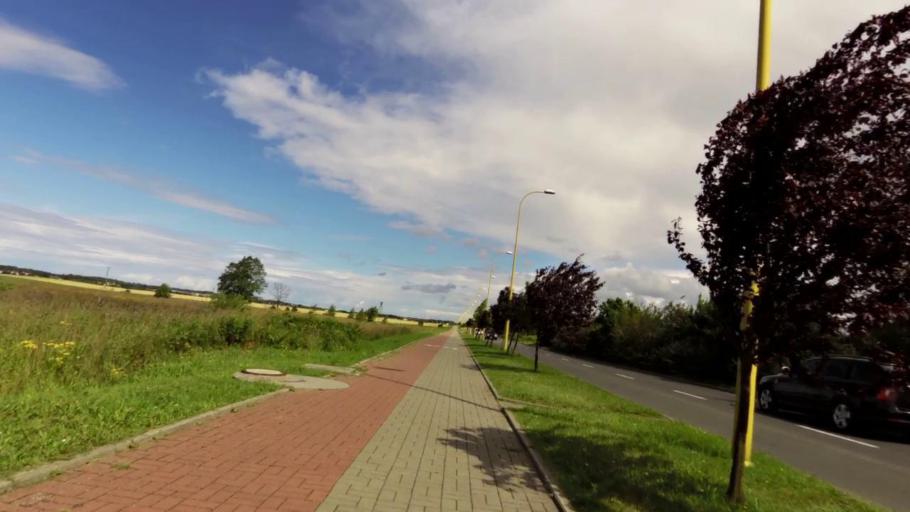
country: PL
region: West Pomeranian Voivodeship
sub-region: Powiat slawienski
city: Darlowo
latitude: 54.4303
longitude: 16.4134
